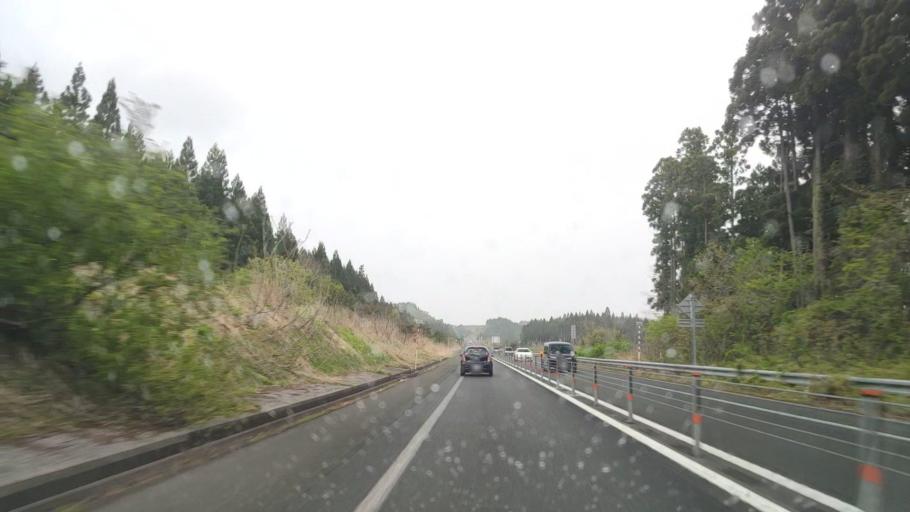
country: JP
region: Akita
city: Noshiromachi
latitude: 40.2087
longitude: 140.1802
